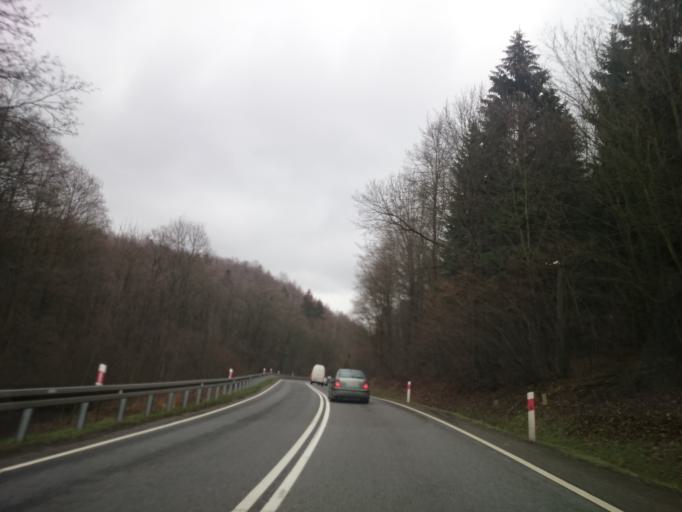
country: PL
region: Lower Silesian Voivodeship
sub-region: Powiat zabkowicki
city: Zloty Stok
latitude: 50.4378
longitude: 16.7958
